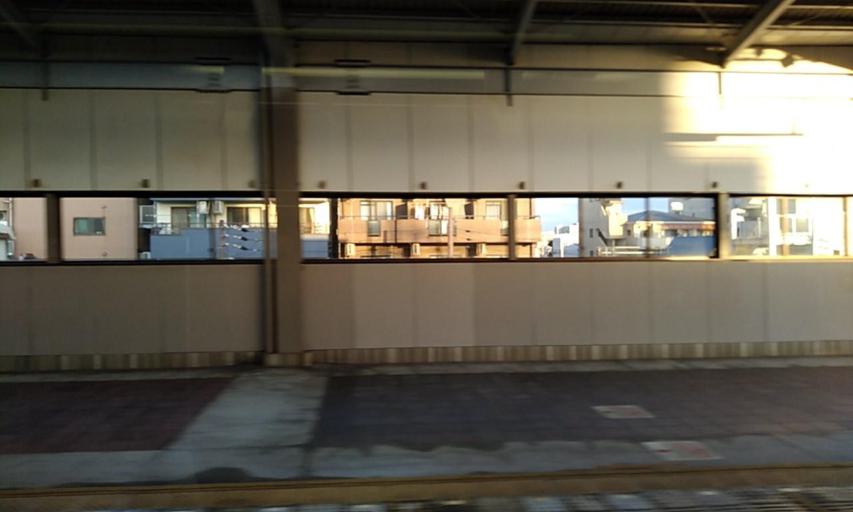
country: JP
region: Osaka
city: Osaka-shi
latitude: 34.6366
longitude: 135.4967
